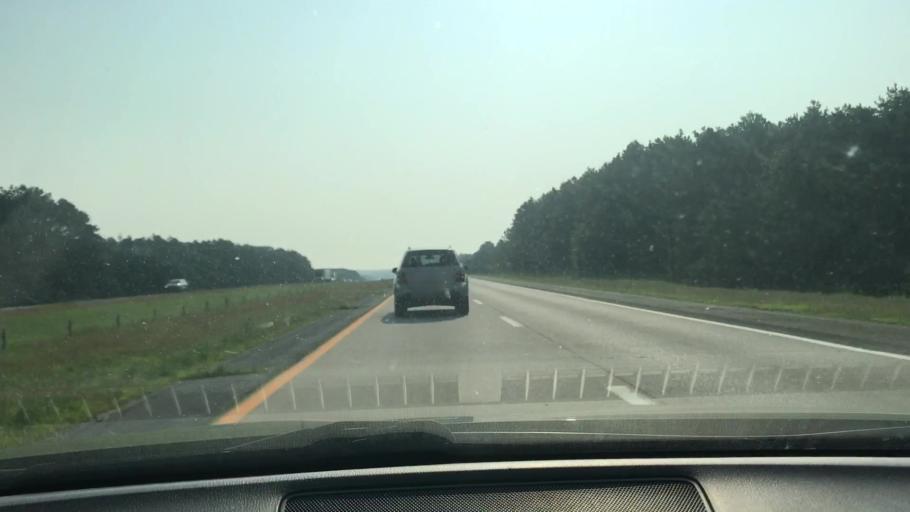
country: US
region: New York
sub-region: Suffolk County
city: East Quogue
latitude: 40.8754
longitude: -72.5779
